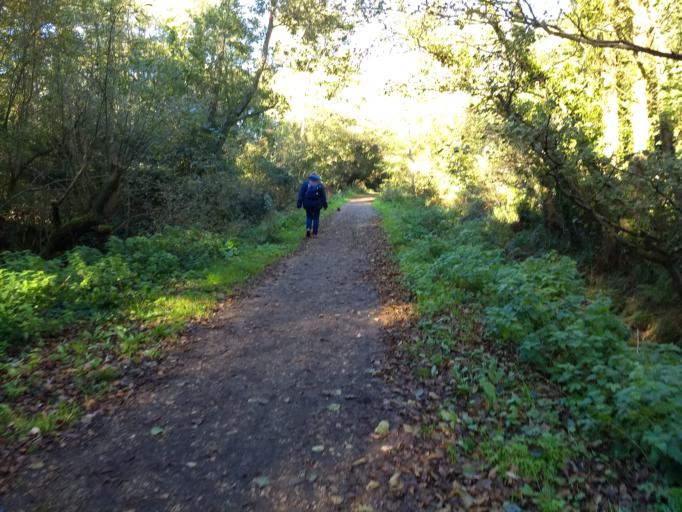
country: GB
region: England
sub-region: Isle of Wight
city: Newport
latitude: 50.6796
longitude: -1.2893
